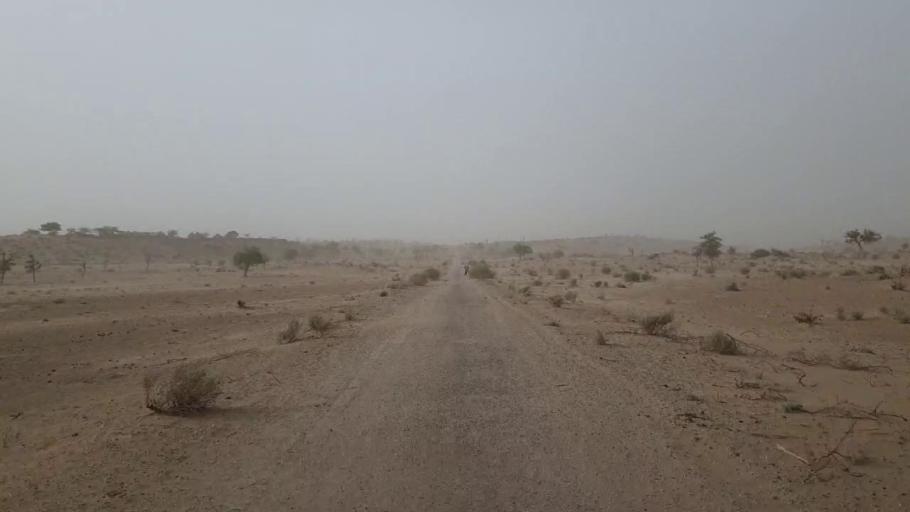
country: PK
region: Sindh
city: Islamkot
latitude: 24.5524
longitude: 70.3604
